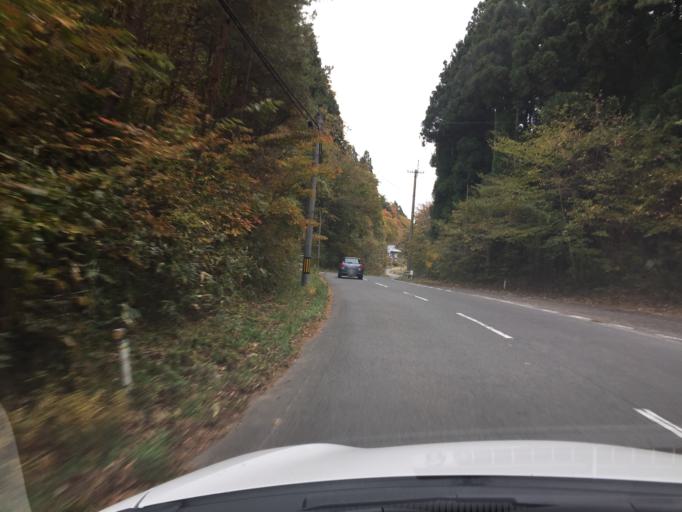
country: JP
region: Fukushima
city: Iwaki
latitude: 37.1862
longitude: 140.7121
